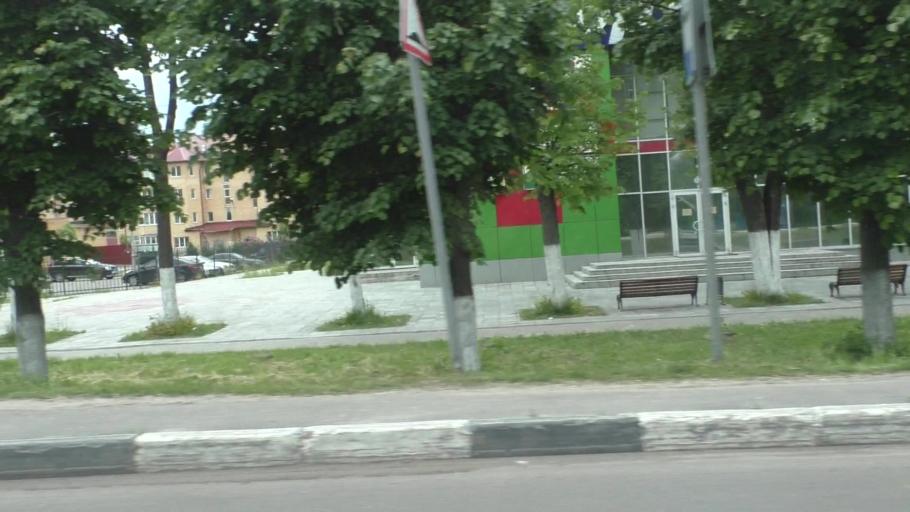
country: RU
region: Moskovskaya
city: Yegor'yevsk
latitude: 55.3937
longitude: 39.0200
